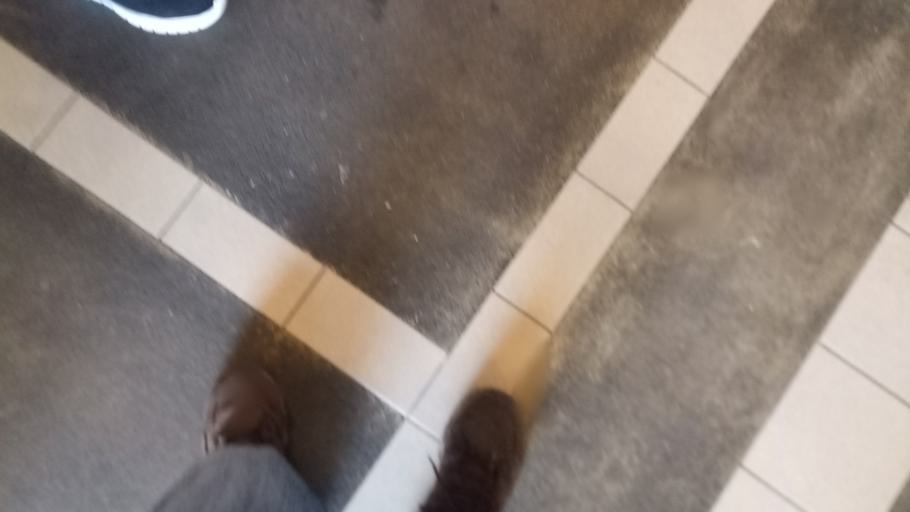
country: PT
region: Azores
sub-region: Angra do Heroismo
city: Angra do Heroismo
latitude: 38.6808
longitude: -27.3155
